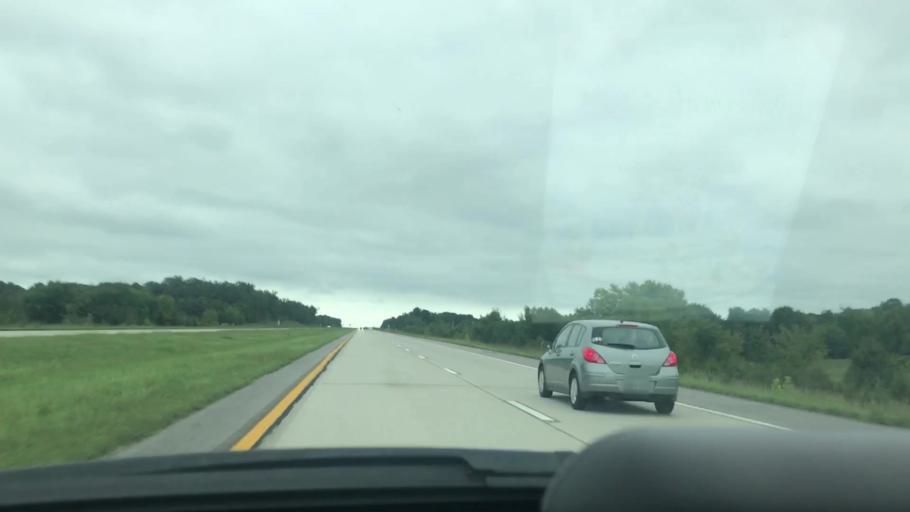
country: US
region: Missouri
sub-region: Greene County
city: Fair Grove
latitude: 37.4684
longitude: -93.1395
